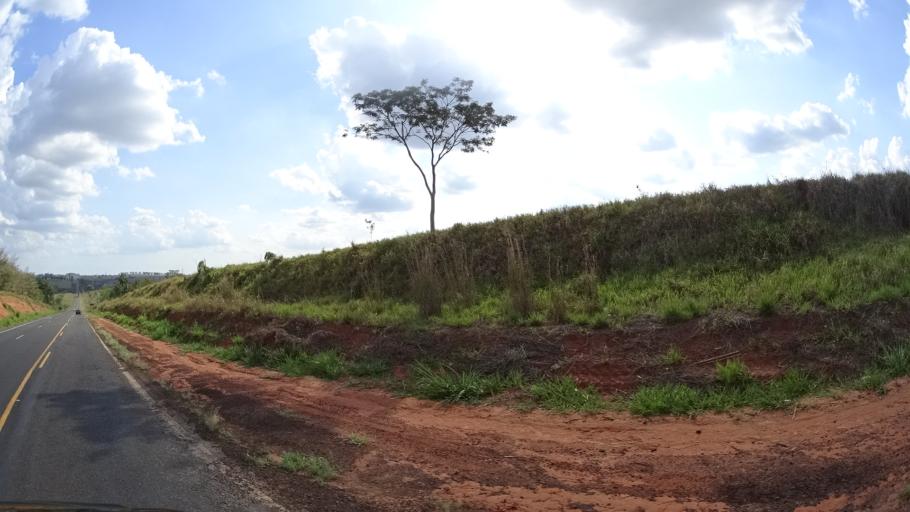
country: BR
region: Sao Paulo
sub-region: Urupes
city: Urupes
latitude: -21.1222
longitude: -49.2720
